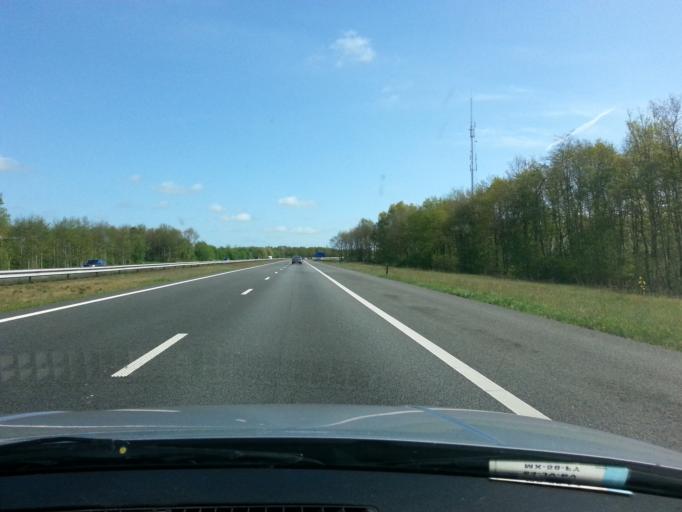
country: NL
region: Friesland
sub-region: Gemeente Smallingerland
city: Boornbergum
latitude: 53.0815
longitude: 6.0721
